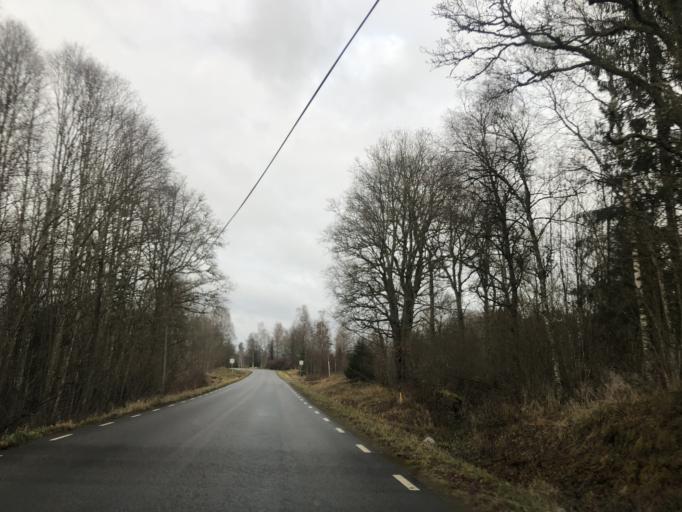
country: SE
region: Vaestra Goetaland
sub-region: Ulricehamns Kommun
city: Ulricehamn
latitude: 57.8323
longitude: 13.2596
